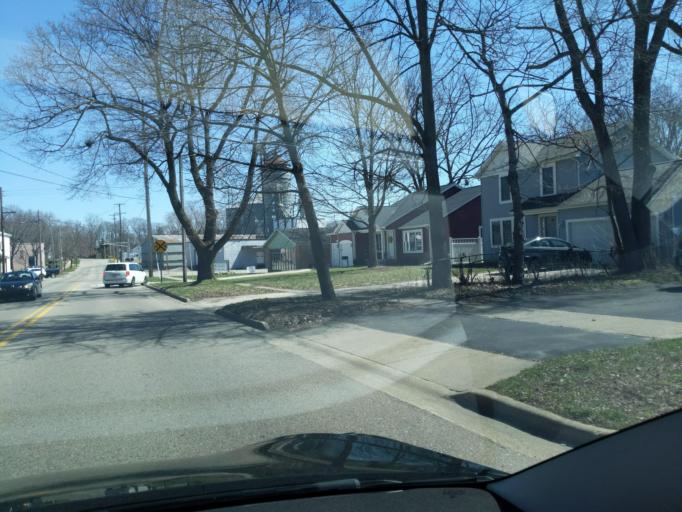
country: US
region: Michigan
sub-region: Ingham County
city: Mason
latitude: 42.5822
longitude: -84.4497
